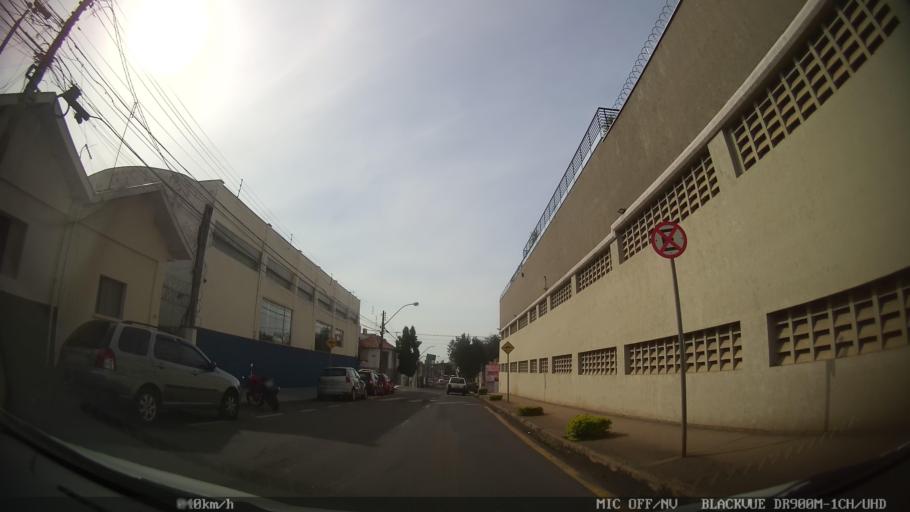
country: BR
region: Sao Paulo
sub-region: Piracicaba
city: Piracicaba
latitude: -22.7355
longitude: -47.6503
